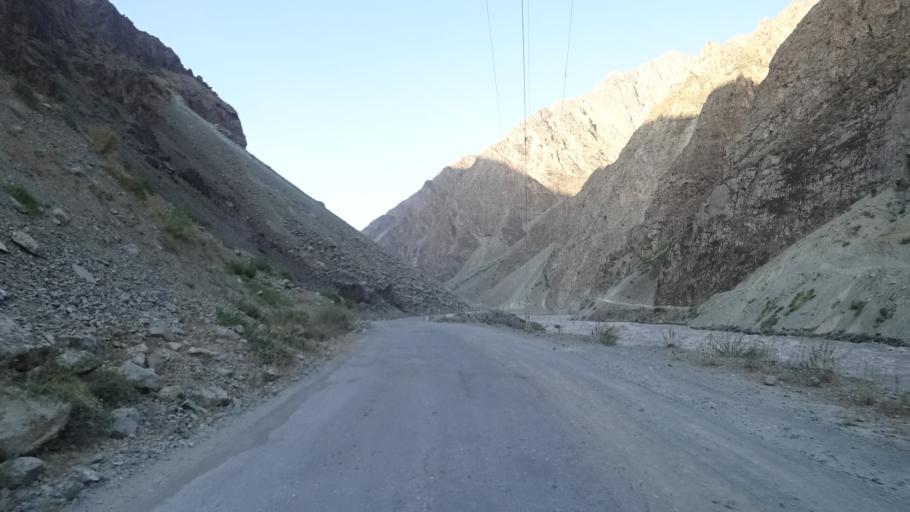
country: TJ
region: Gorno-Badakhshan
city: Qalaikhumb
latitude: 38.4241
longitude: 70.7472
